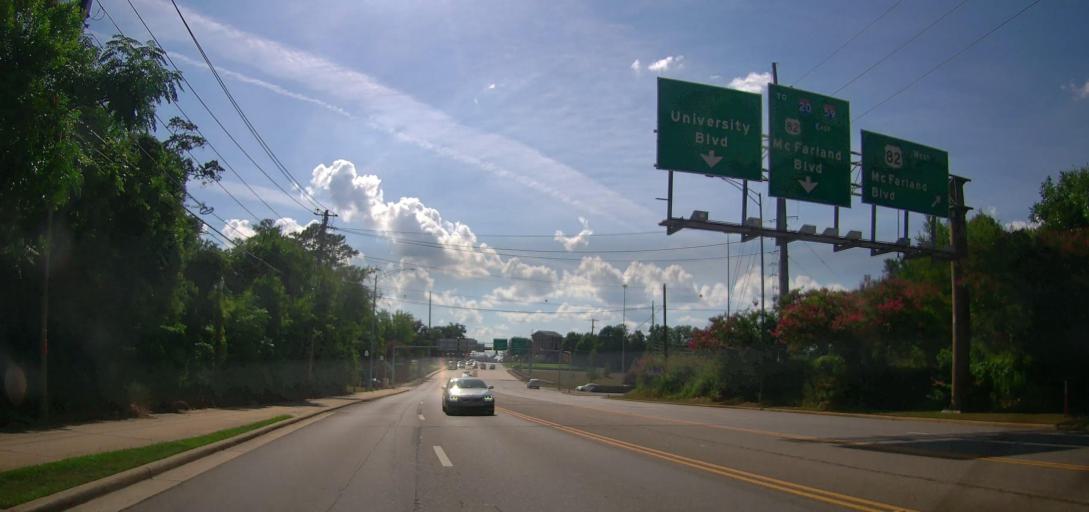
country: US
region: Alabama
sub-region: Tuscaloosa County
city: Tuscaloosa
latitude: 33.2060
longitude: -87.5223
